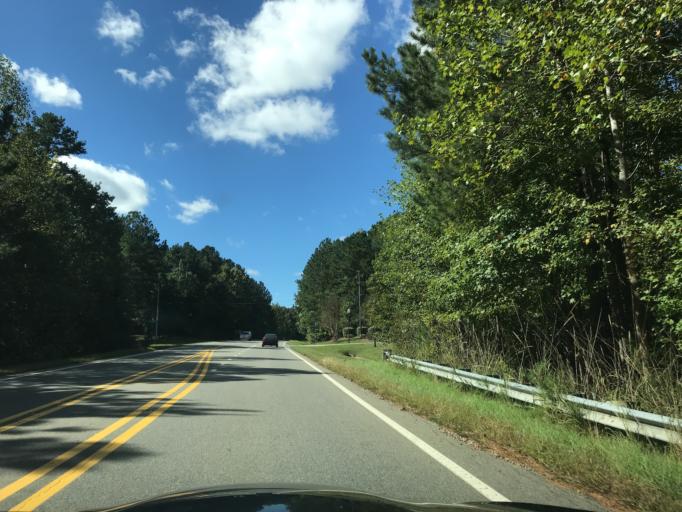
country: US
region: North Carolina
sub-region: Durham County
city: Gorman
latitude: 35.9853
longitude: -78.7060
